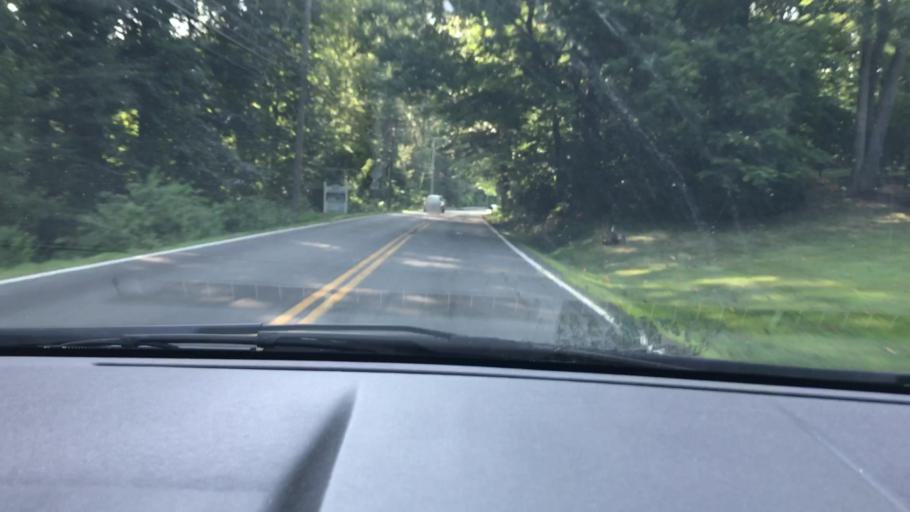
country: US
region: Virginia
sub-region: Fairfax County
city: Tysons Corner
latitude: 38.9585
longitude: -77.2367
